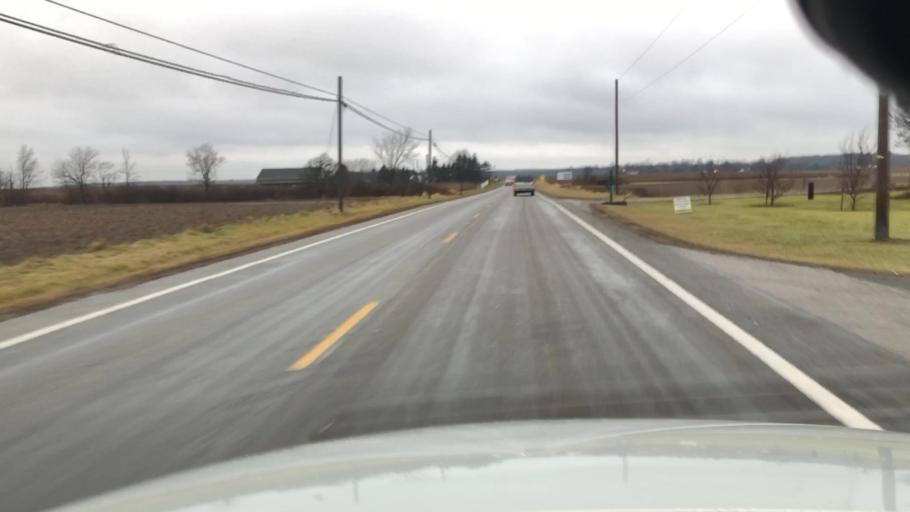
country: US
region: Ohio
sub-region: Allen County
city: Lima
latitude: 40.7073
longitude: -84.0052
